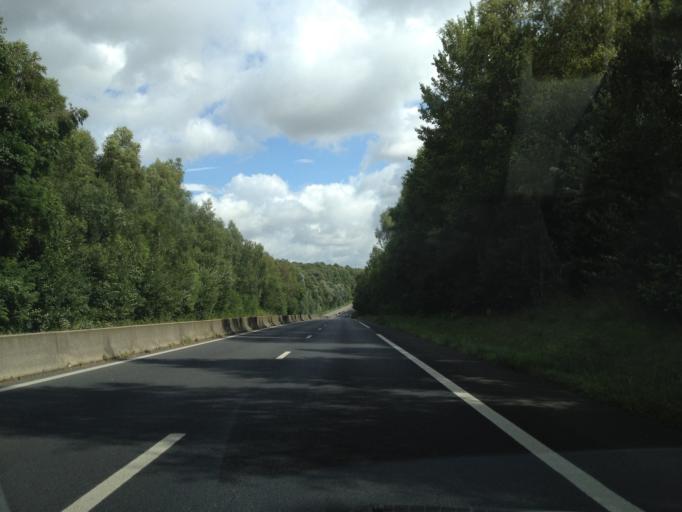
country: FR
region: Haute-Normandie
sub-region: Departement de la Seine-Maritime
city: Isneauville
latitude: 49.5045
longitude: 1.1773
